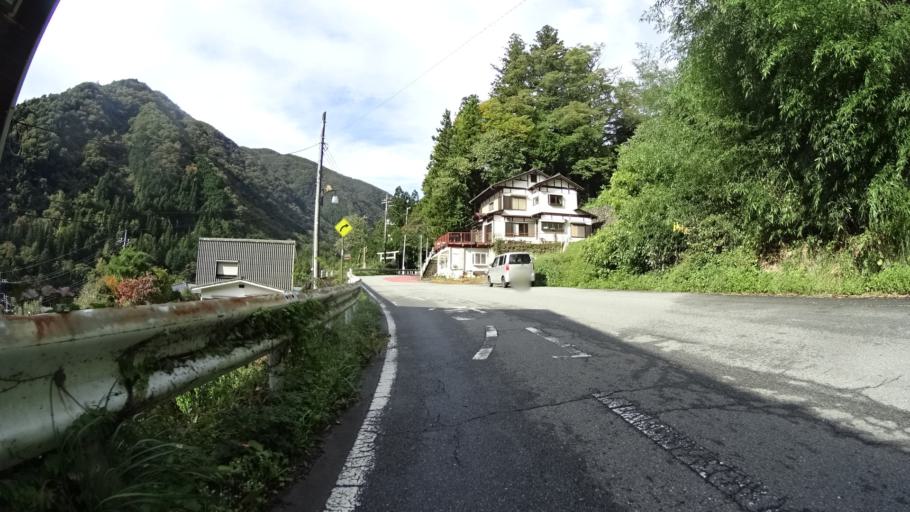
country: JP
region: Yamanashi
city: Otsuki
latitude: 35.7942
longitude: 138.9138
